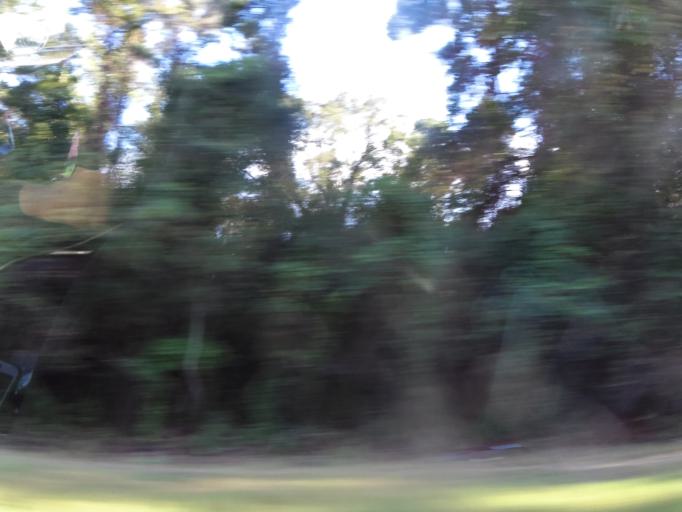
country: US
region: Georgia
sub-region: Brooks County
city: Quitman
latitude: 30.7874
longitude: -83.5099
